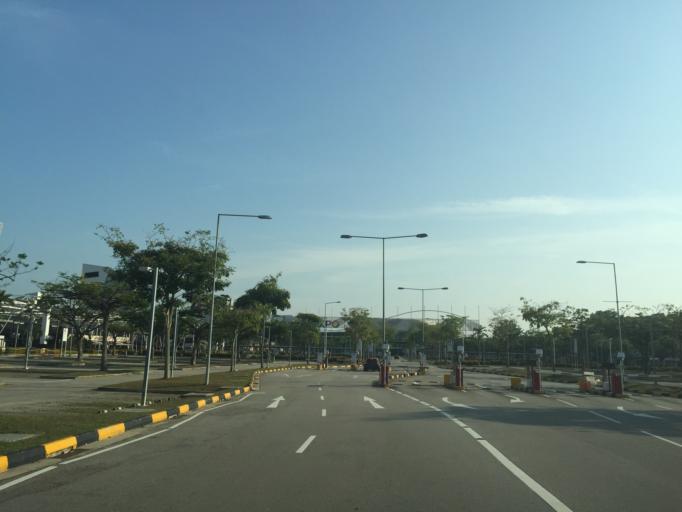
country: SG
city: Singapore
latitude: 1.3365
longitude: 103.9604
